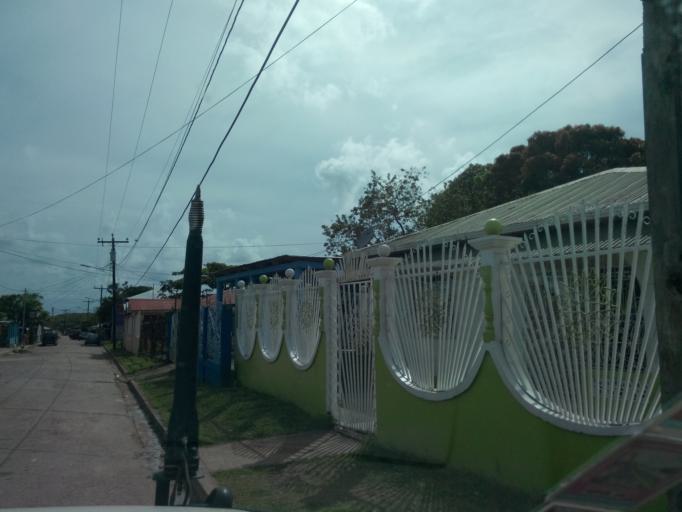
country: NI
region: Atlantico Sur
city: Bluefields
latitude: 11.9965
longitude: -83.7697
